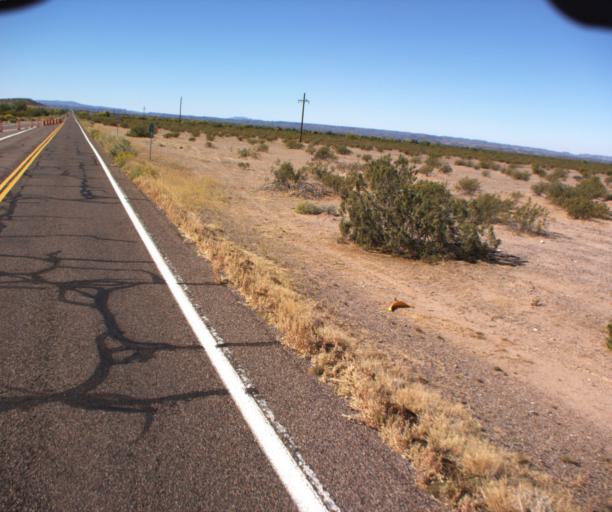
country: US
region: Arizona
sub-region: Maricopa County
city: Gila Bend
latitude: 32.7140
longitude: -112.8427
